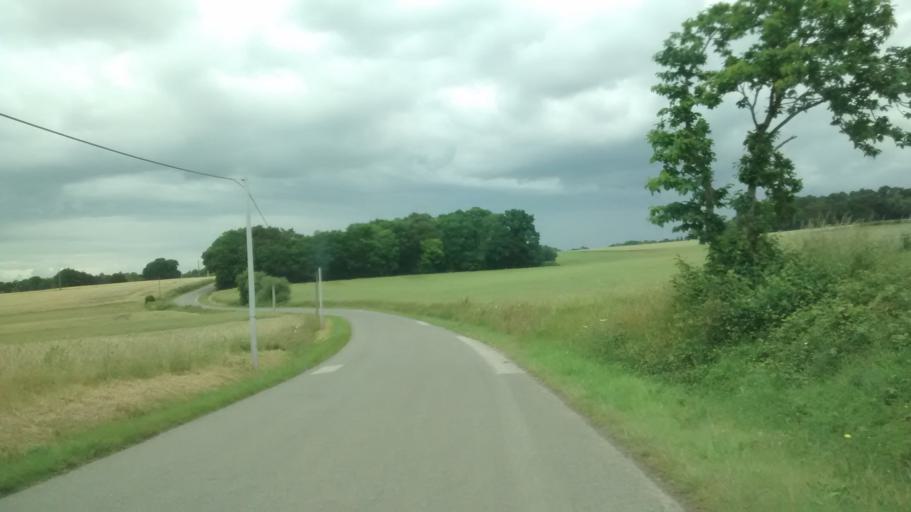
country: FR
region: Brittany
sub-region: Departement d'Ille-et-Vilaine
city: Sixt-sur-Aff
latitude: 47.7869
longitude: -2.1059
